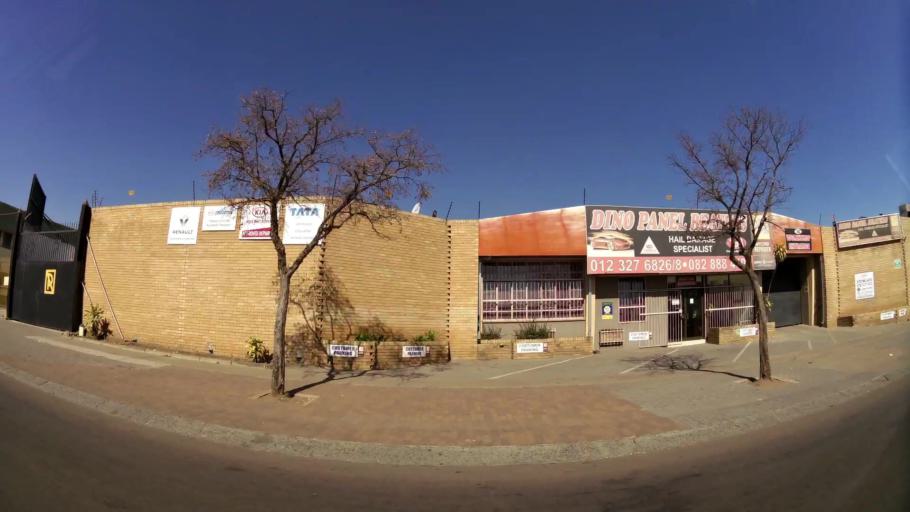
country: ZA
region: Gauteng
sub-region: City of Tshwane Metropolitan Municipality
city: Pretoria
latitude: -25.7542
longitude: 28.1684
